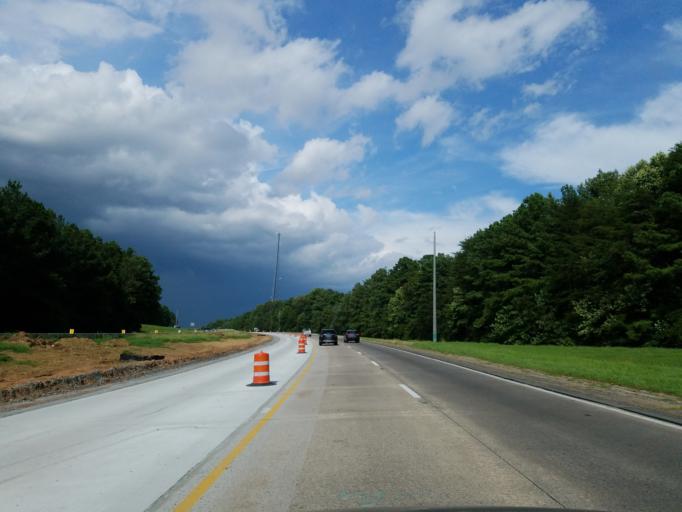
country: US
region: Georgia
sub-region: Forsyth County
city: Cumming
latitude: 34.1586
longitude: -84.1709
